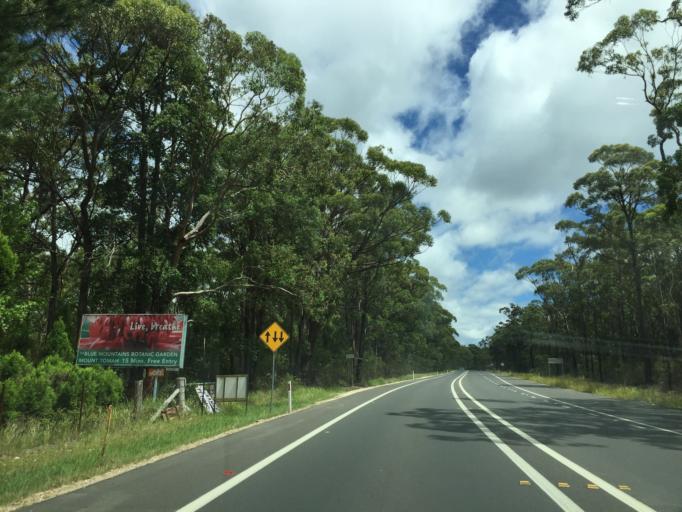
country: AU
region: New South Wales
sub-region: Hawkesbury
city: Richmond
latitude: -33.5136
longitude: 150.5745
